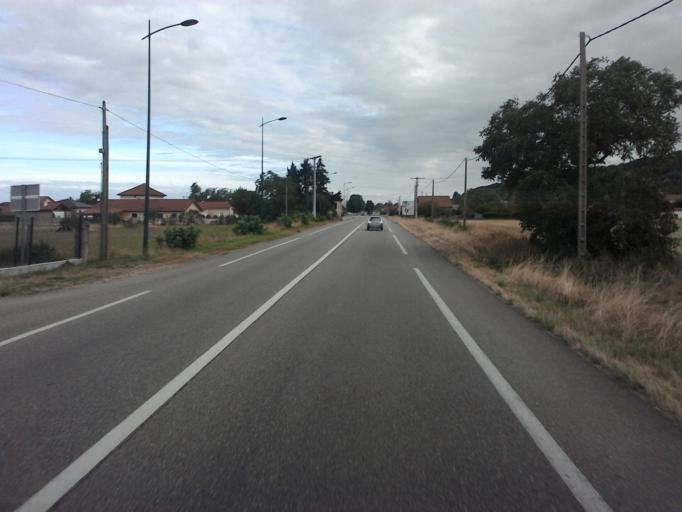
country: FR
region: Rhone-Alpes
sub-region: Departement de l'Ain
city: Saint-Denis-en-Bugey
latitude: 45.9372
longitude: 5.3340
